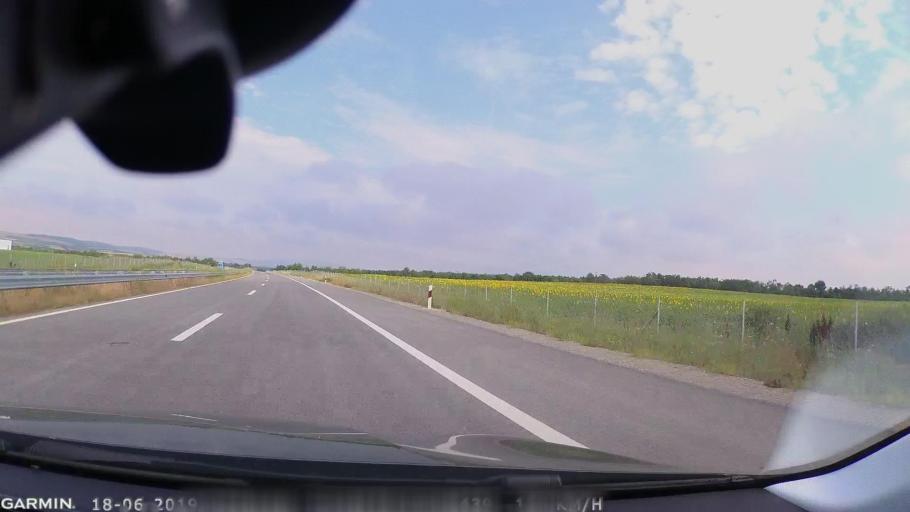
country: MK
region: Sveti Nikole
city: Sveti Nikole
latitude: 41.8277
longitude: 22.0042
